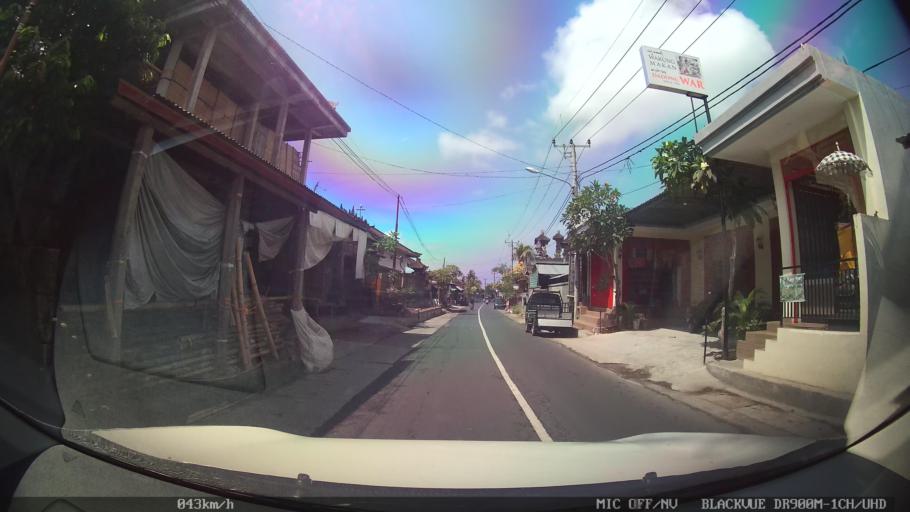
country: ID
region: Bali
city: Banjar Pasekan
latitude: -8.6009
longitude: 115.2916
